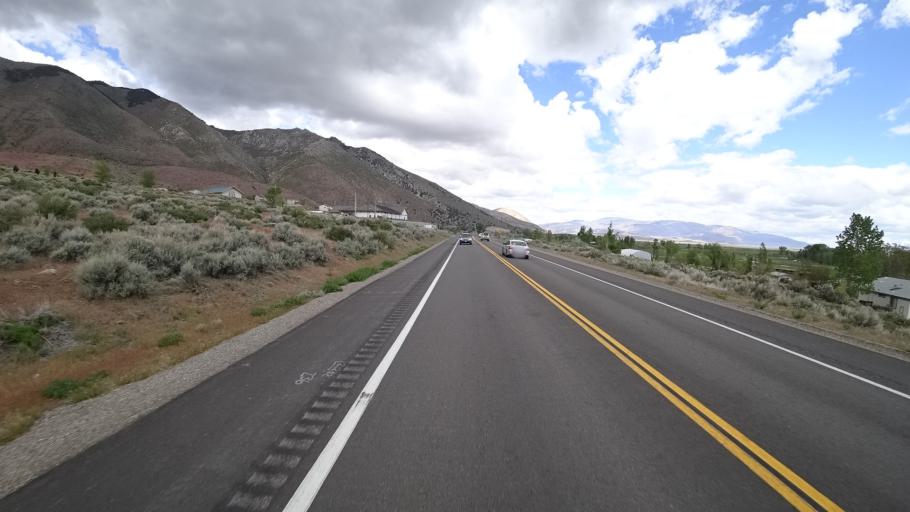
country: US
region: Nevada
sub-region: Lyon County
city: Smith Valley
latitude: 38.5851
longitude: -119.5135
